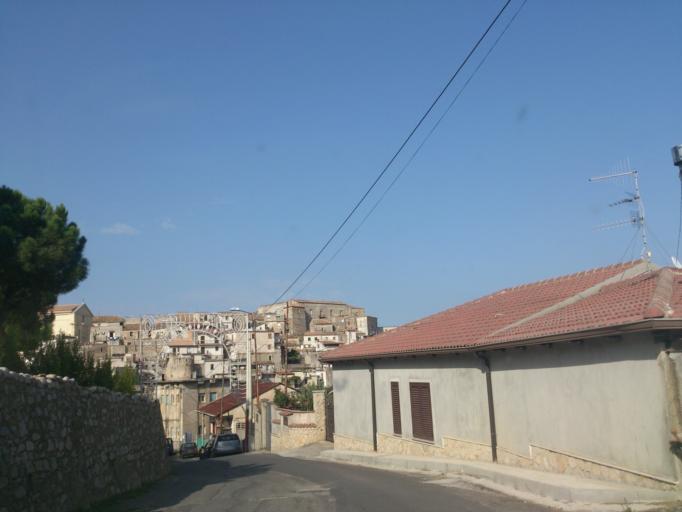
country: IT
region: Calabria
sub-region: Provincia di Reggio Calabria
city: Monasterace
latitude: 38.4521
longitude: 16.5497
